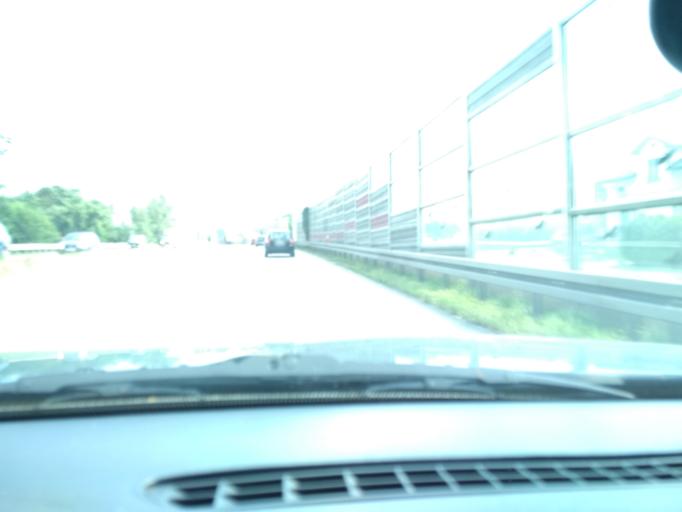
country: PL
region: Silesian Voivodeship
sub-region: Zory
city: Zory
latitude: 50.0176
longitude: 18.7074
